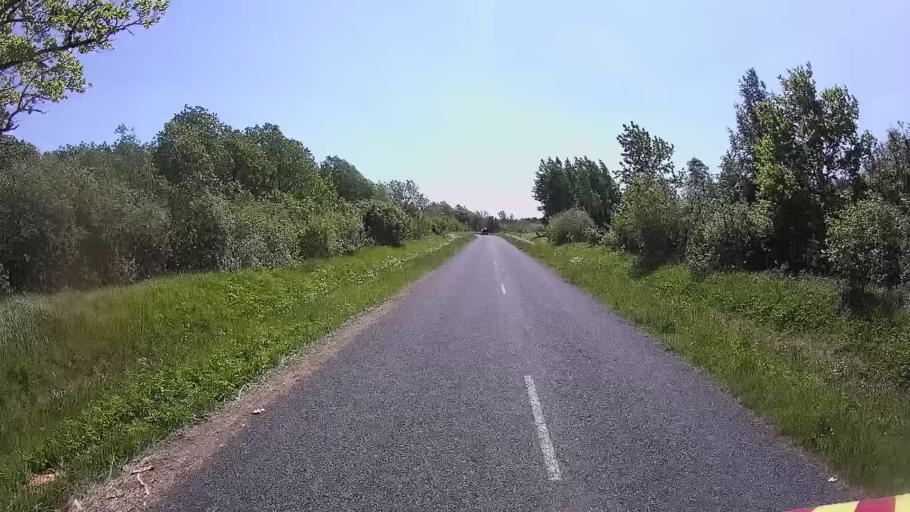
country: LV
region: Dundaga
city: Dundaga
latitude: 57.9387
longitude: 22.0907
